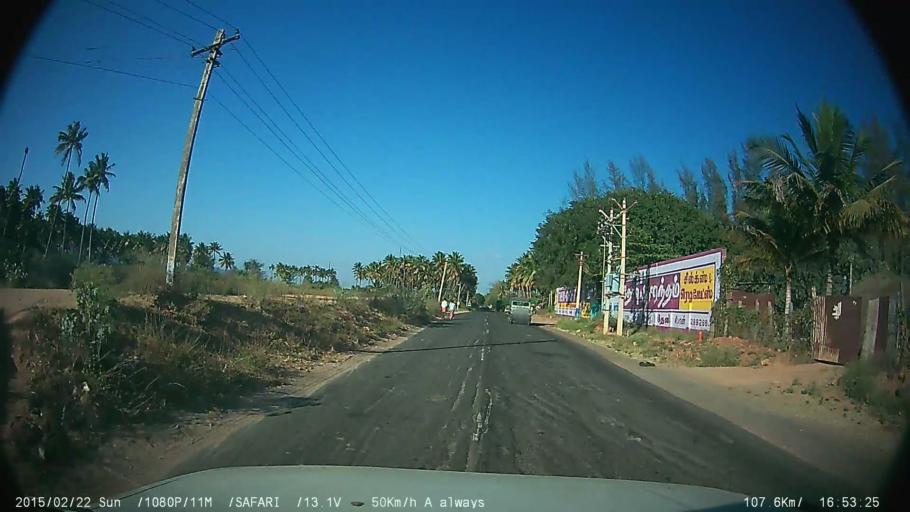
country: IN
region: Tamil Nadu
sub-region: Theni
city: Gudalur
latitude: 9.6647
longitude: 77.2310
